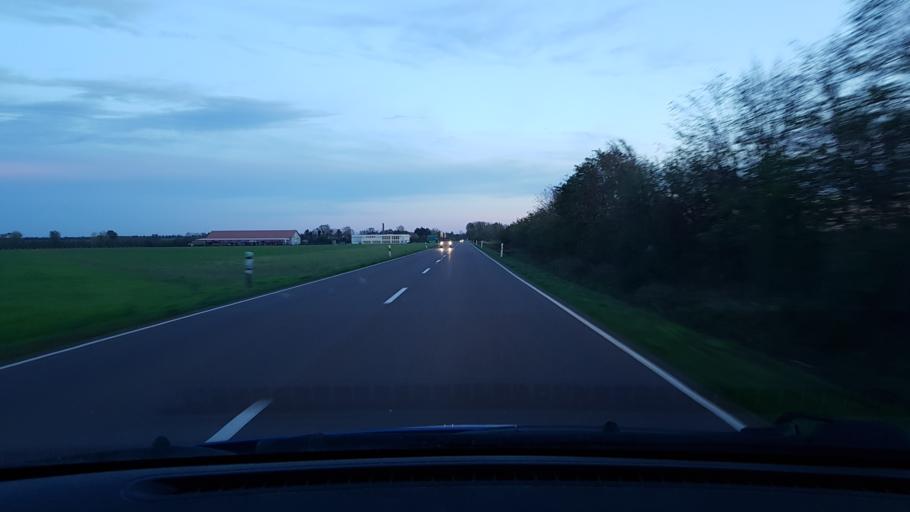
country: DE
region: Saxony-Anhalt
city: Leitzkau
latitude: 52.0246
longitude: 12.0017
